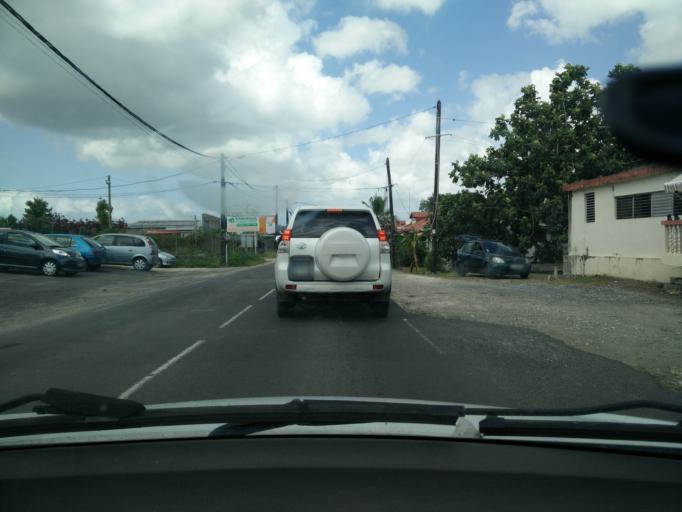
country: GP
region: Guadeloupe
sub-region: Guadeloupe
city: Les Abymes
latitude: 16.2603
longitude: -61.5068
